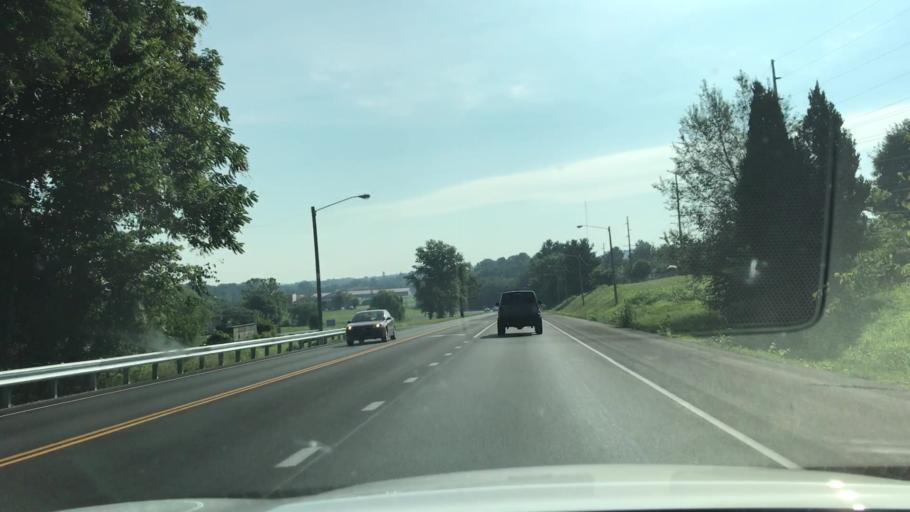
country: US
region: Kentucky
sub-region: Barren County
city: Glasgow
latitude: 37.0151
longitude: -85.9133
